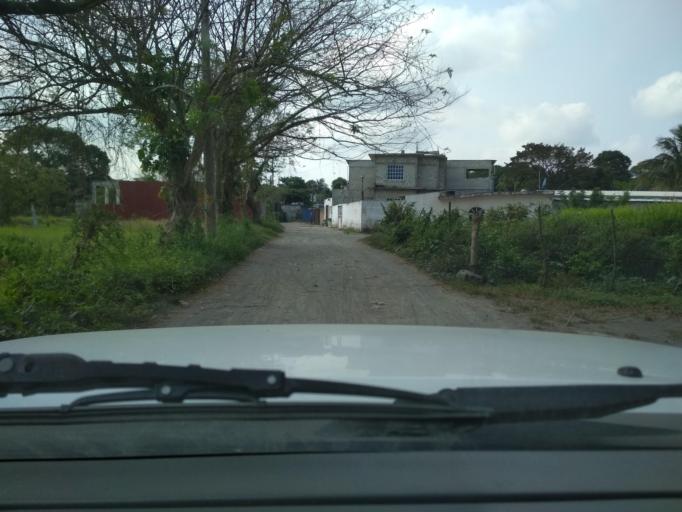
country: MX
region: Veracruz
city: El Tejar
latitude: 19.0809
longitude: -96.1633
